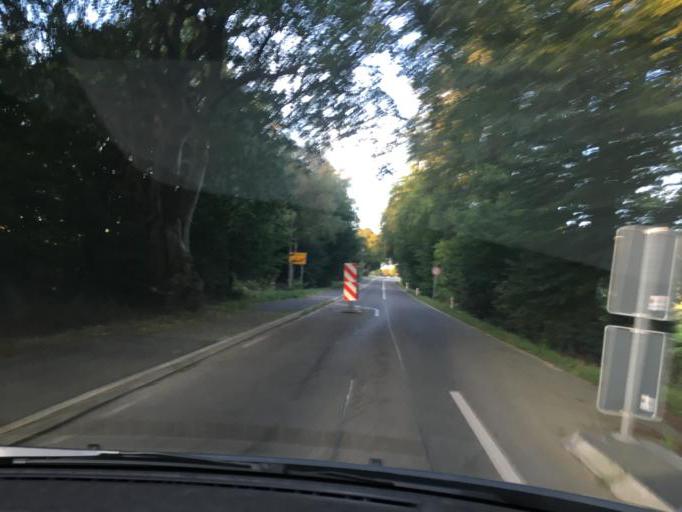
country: DE
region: North Rhine-Westphalia
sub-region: Regierungsbezirk Koln
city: Simmerath
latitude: 50.6252
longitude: 6.3100
